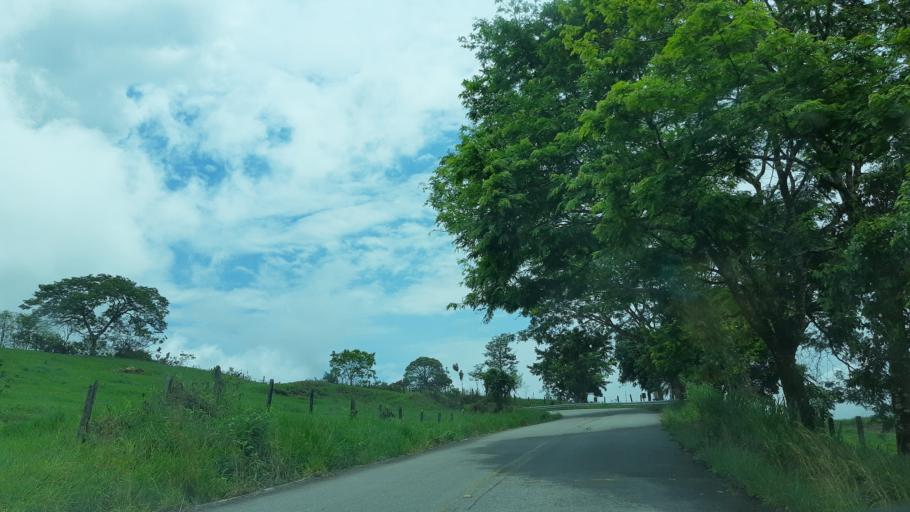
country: CO
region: Casanare
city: Sabanalarga
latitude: 4.8239
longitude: -73.0549
